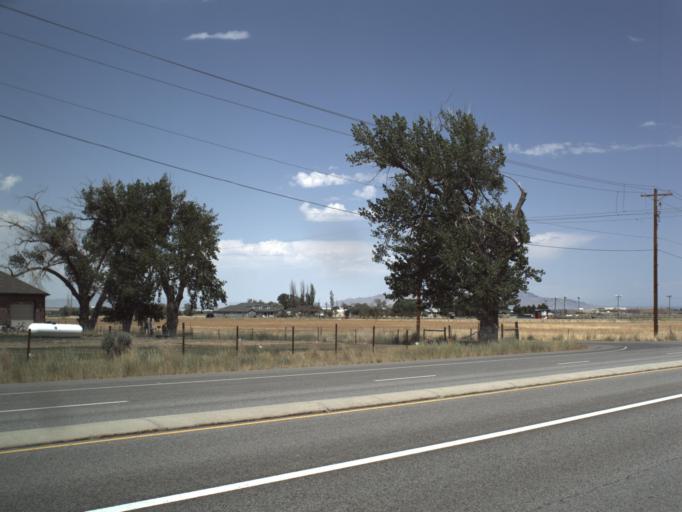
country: US
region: Utah
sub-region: Tooele County
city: Erda
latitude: 40.6091
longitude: -112.2943
